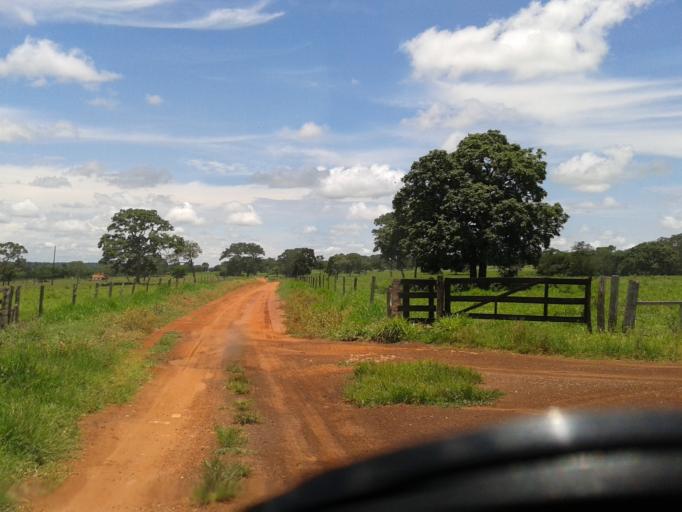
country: BR
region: Minas Gerais
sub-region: Santa Vitoria
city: Santa Vitoria
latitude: -18.9594
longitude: -49.8653
